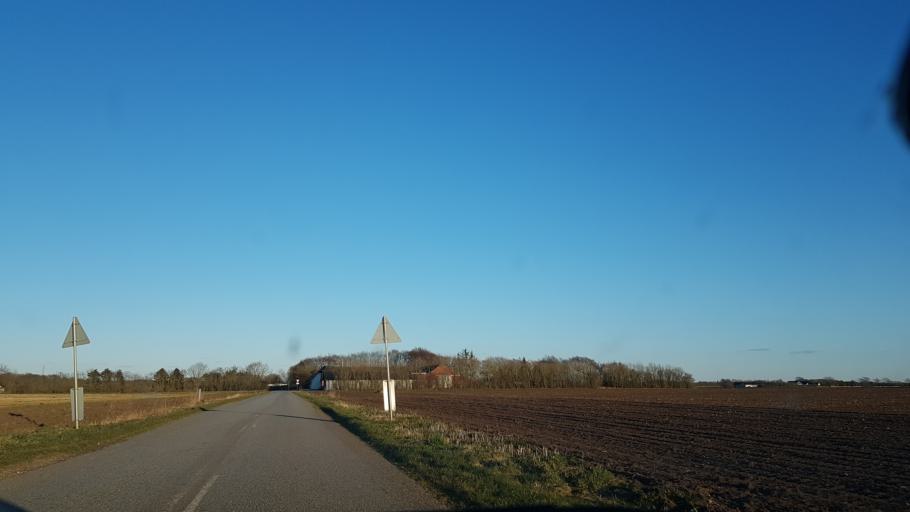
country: DK
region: South Denmark
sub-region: Esbjerg Kommune
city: Ribe
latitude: 55.3839
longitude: 8.7484
